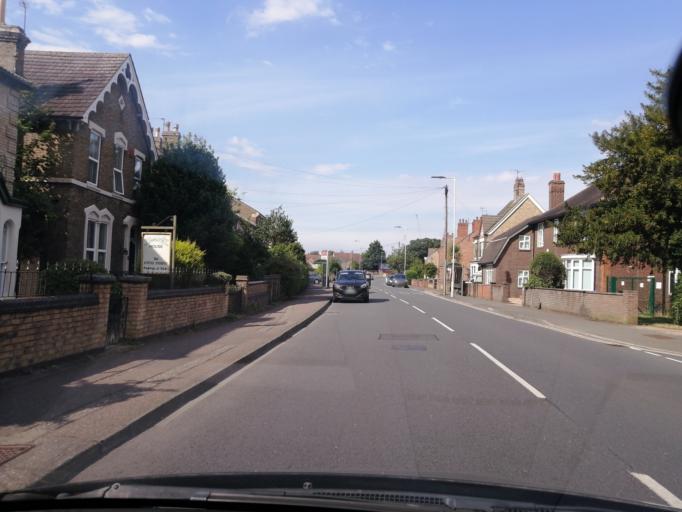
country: GB
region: England
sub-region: Peterborough
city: Peterborough
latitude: 52.5615
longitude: -0.2450
